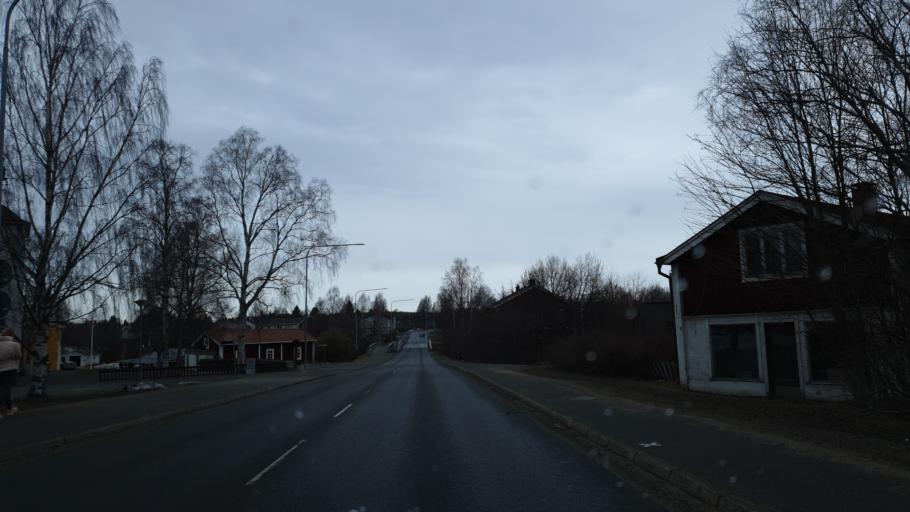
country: SE
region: Vaesterbotten
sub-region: Skelleftea Kommun
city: Kage
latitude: 64.8336
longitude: 20.9875
